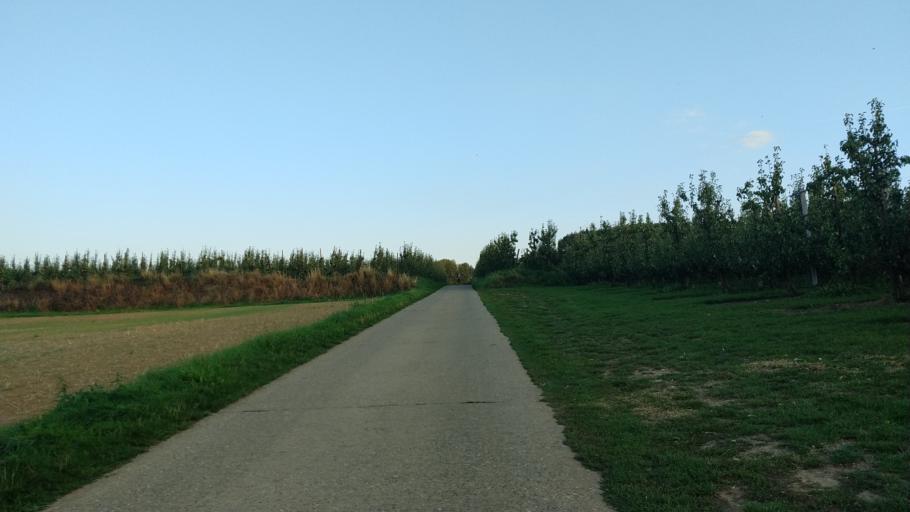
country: BE
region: Flanders
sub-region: Provincie Vlaams-Brabant
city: Lubbeek
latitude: 50.8900
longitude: 4.8185
